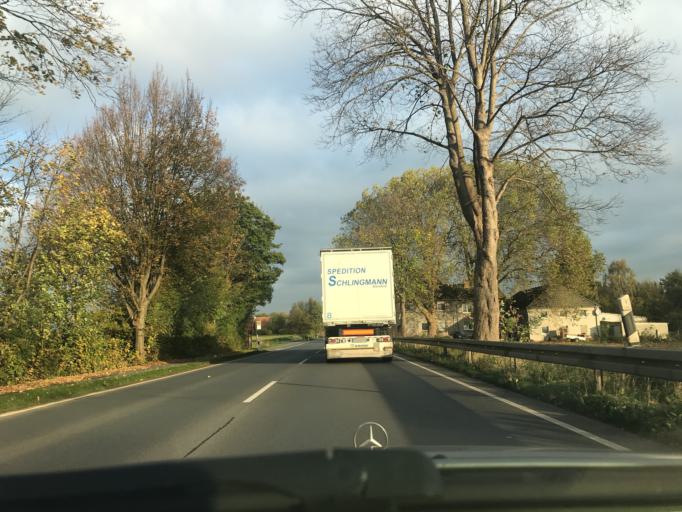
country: DE
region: North Rhine-Westphalia
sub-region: Regierungsbezirk Arnsberg
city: Soest
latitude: 51.6241
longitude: 8.1013
